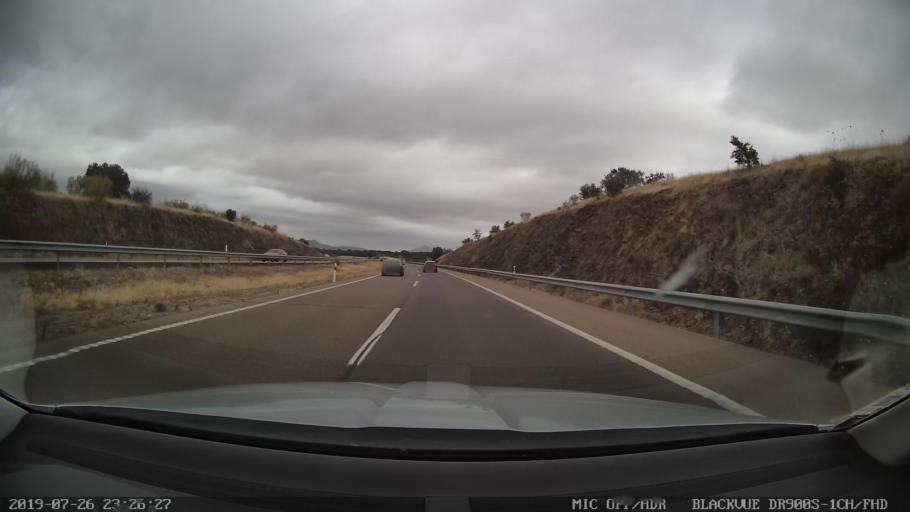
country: ES
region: Extremadura
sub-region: Provincia de Caceres
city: Villamesias
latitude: 39.2078
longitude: -5.8775
